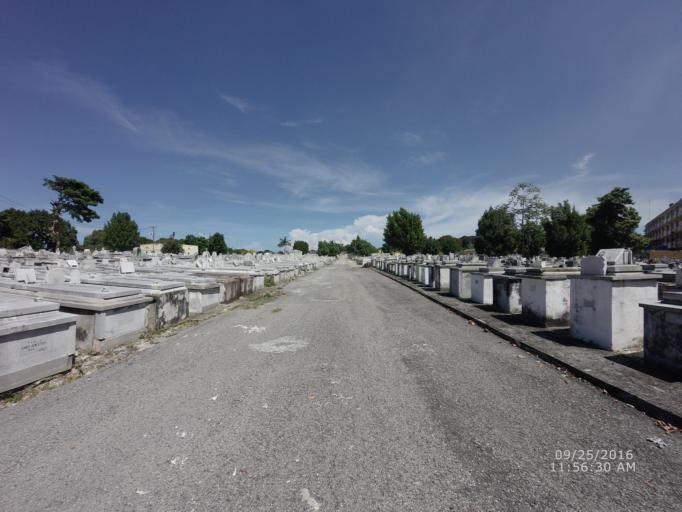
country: CU
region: La Habana
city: Havana
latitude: 23.1202
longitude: -82.3956
